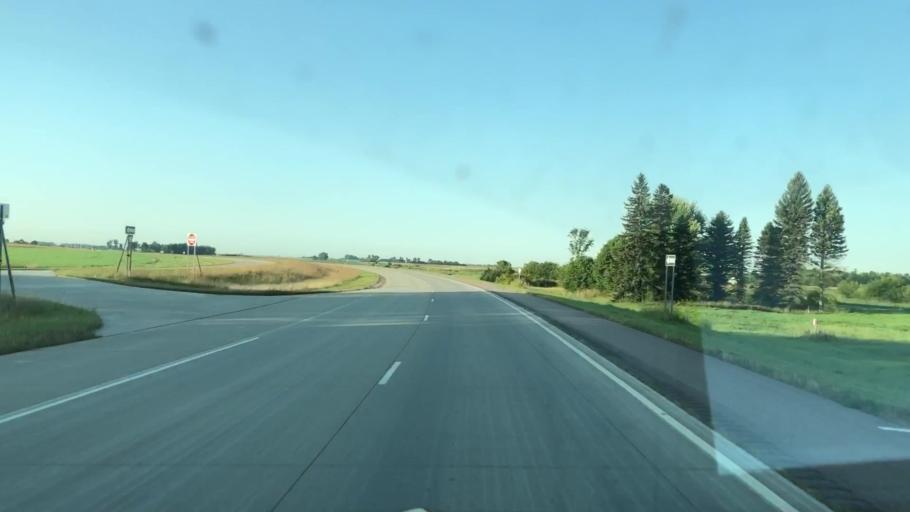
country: US
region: Minnesota
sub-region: Nobles County
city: Worthington
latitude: 43.5782
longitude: -95.6523
